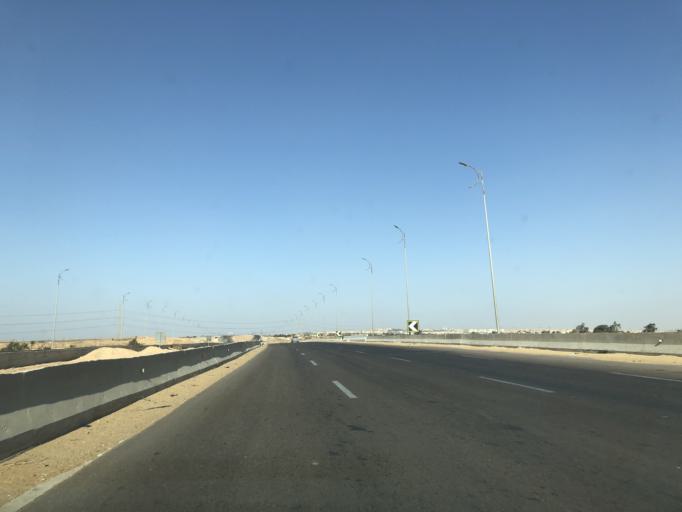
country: EG
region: Al Jizah
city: Awsim
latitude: 30.0687
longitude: 30.9054
